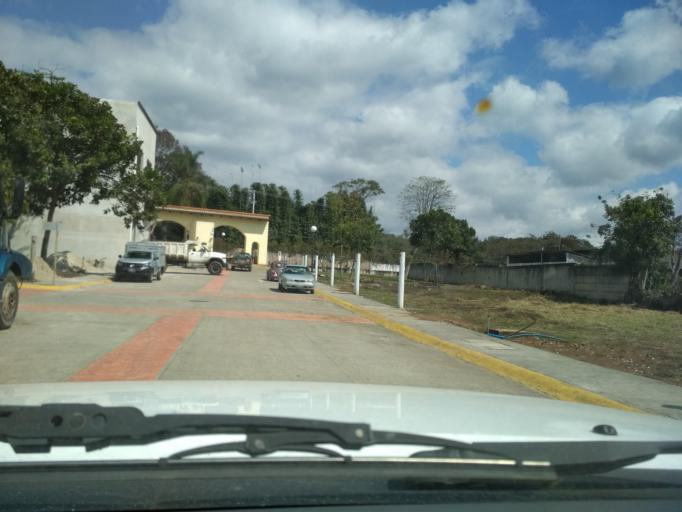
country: MX
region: Veracruz
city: Coatepec
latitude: 19.4502
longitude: -96.9482
